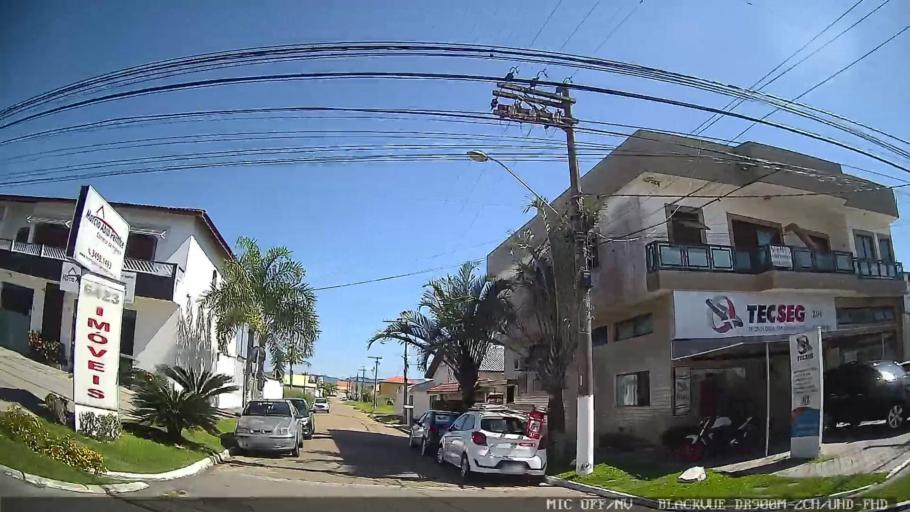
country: BR
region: Sao Paulo
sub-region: Peruibe
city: Peruibe
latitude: -24.2875
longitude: -46.9582
